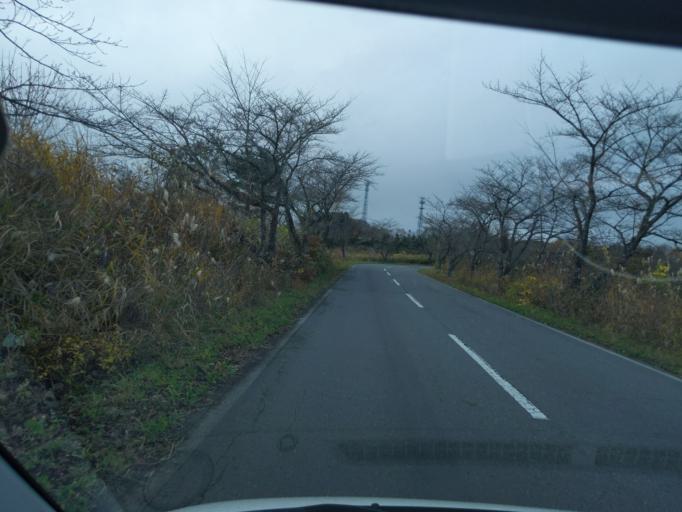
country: JP
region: Iwate
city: Mizusawa
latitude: 39.0416
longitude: 141.0770
